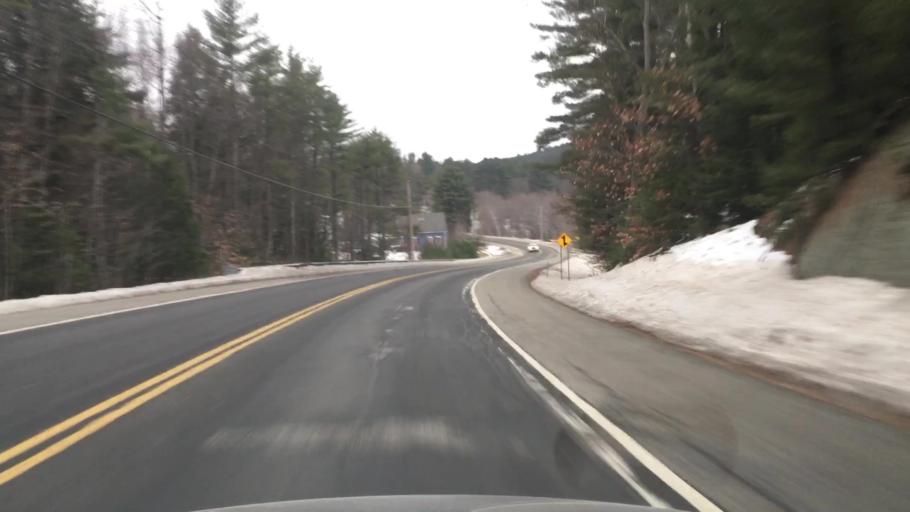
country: US
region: New Hampshire
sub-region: Merrimack County
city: Sutton
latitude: 43.2462
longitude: -71.9237
